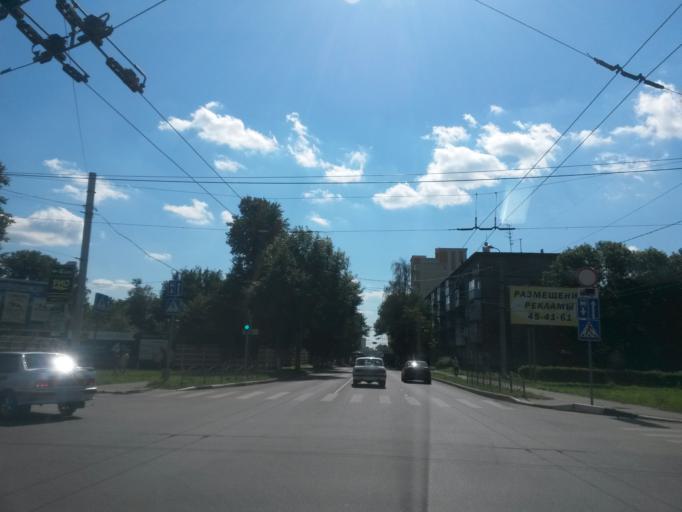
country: RU
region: Ivanovo
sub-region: Gorod Ivanovo
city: Ivanovo
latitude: 56.9878
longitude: 40.9833
